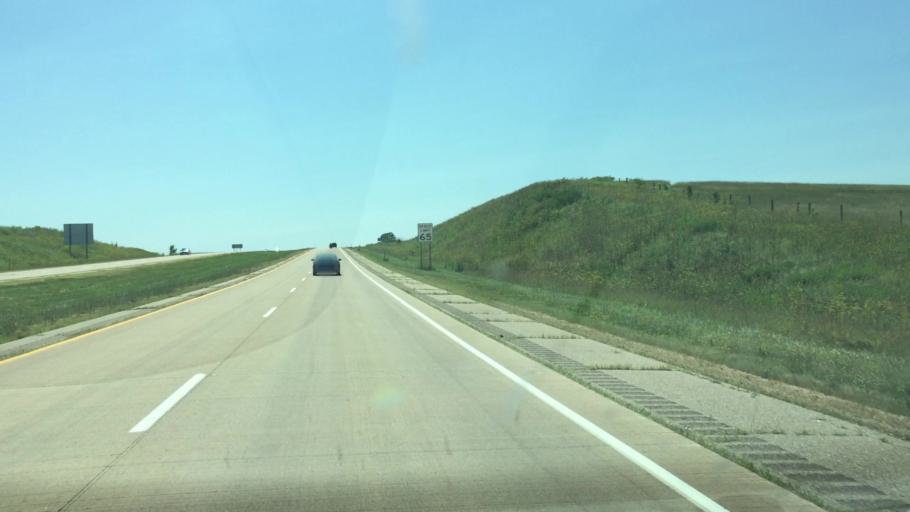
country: US
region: Wisconsin
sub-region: Iowa County
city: Mineral Point
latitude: 42.8823
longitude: -90.1783
